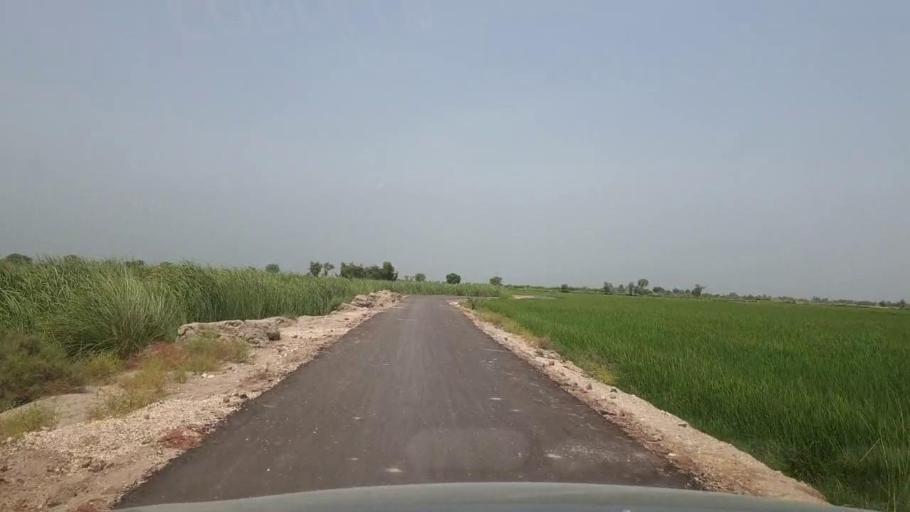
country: PK
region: Sindh
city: Garhi Yasin
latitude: 27.9281
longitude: 68.4329
